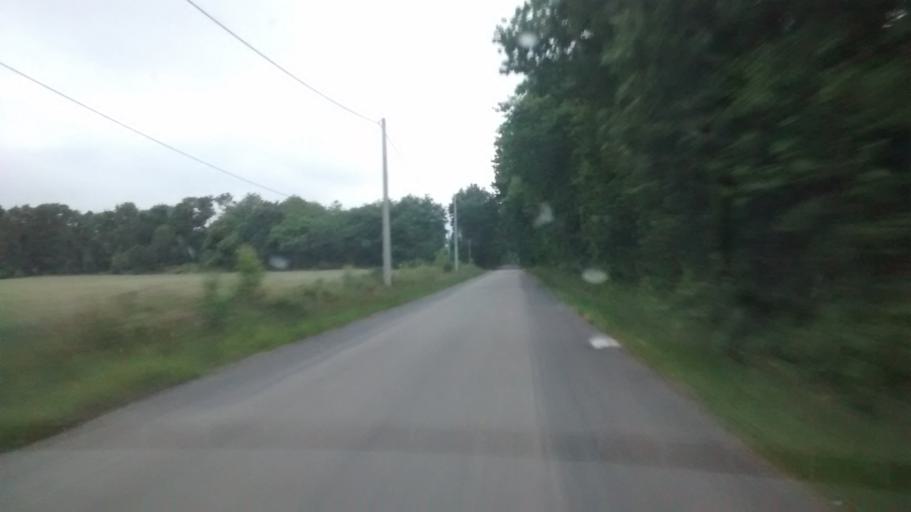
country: FR
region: Brittany
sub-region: Departement du Morbihan
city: Pleucadeuc
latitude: 47.7349
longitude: -2.3362
